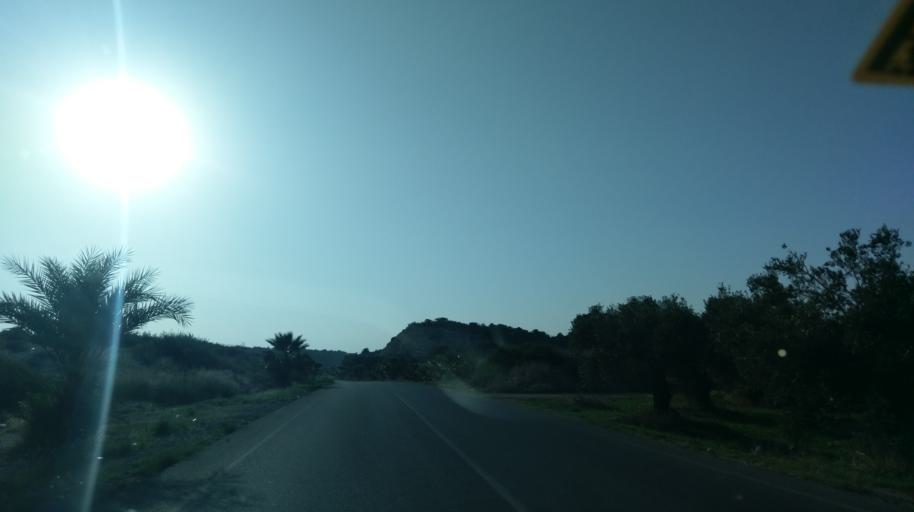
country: CY
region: Ammochostos
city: Leonarisso
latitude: 35.3796
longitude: 34.0599
